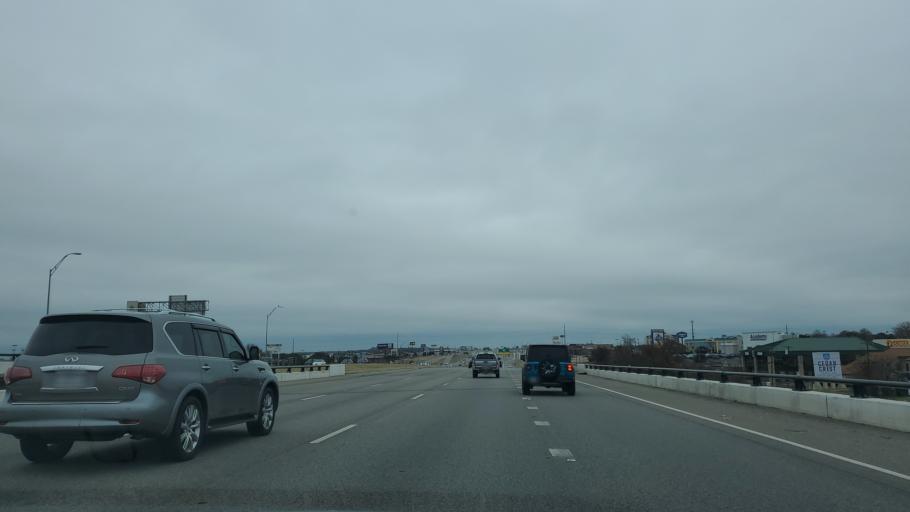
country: US
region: Texas
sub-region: Bell County
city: Killeen
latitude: 31.0910
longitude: -97.7204
